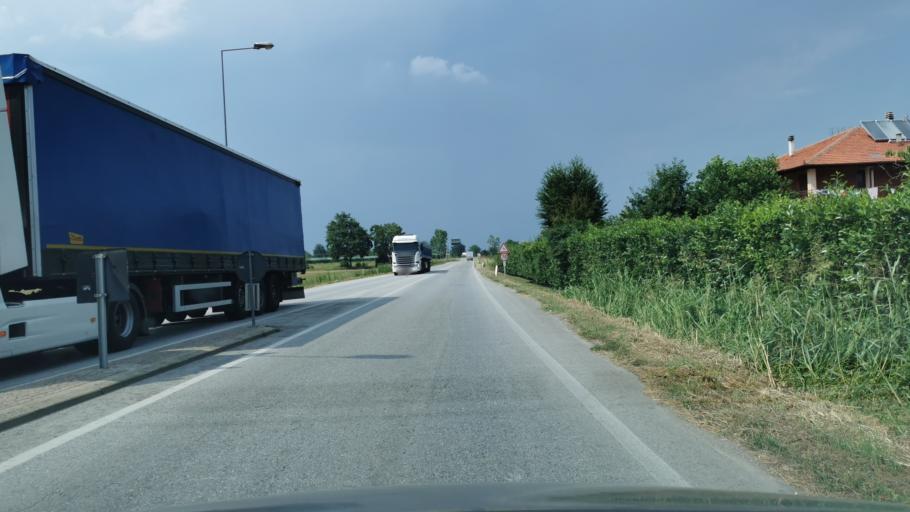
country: IT
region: Piedmont
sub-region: Provincia di Cuneo
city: Villafalletto
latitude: 44.5431
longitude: 7.5480
